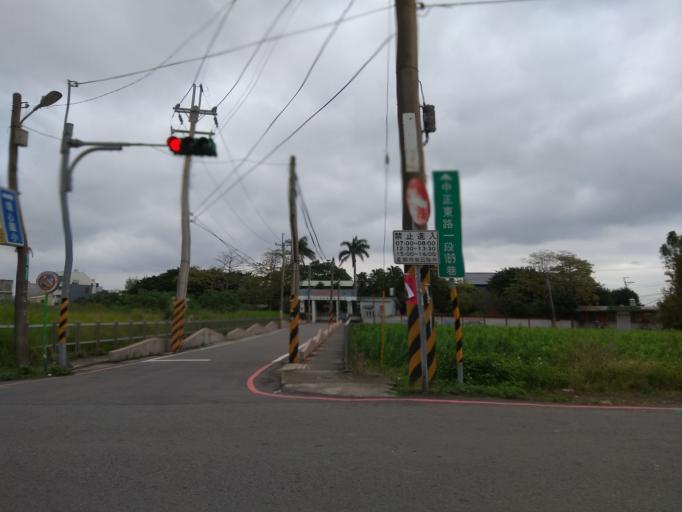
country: TW
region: Taiwan
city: Taoyuan City
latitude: 25.0496
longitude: 121.2240
